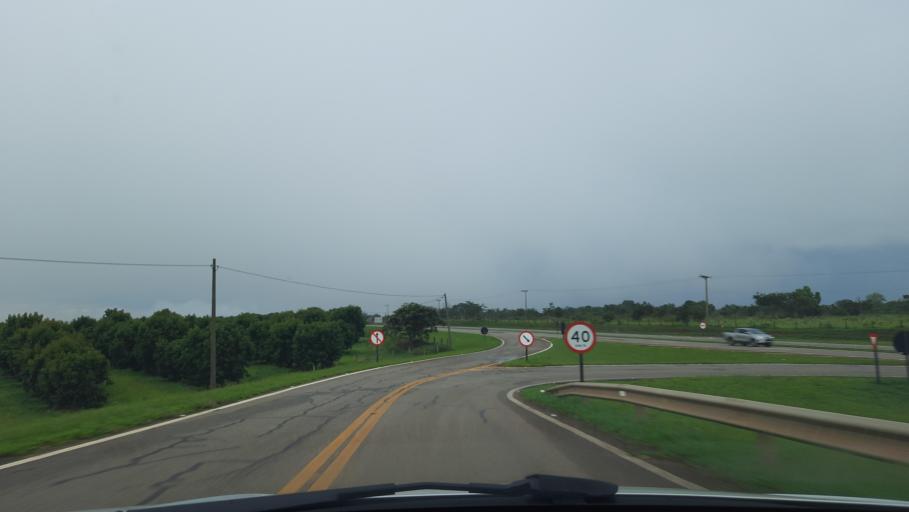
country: BR
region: Sao Paulo
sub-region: Casa Branca
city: Casa Branca
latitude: -21.7480
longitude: -47.0723
